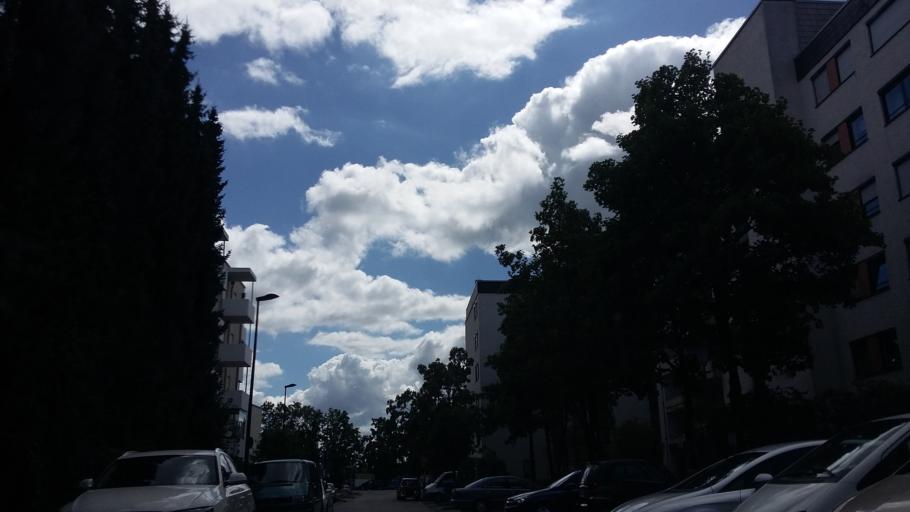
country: DE
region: Bavaria
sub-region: Upper Bavaria
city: Germering
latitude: 48.1342
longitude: 11.3788
